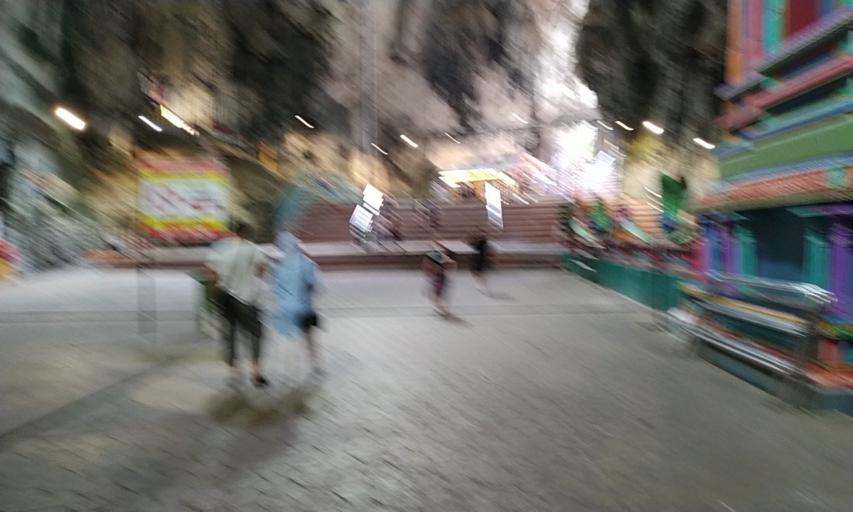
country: MY
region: Kuala Lumpur
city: Kuala Lumpur
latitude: 3.2387
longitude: 101.6856
